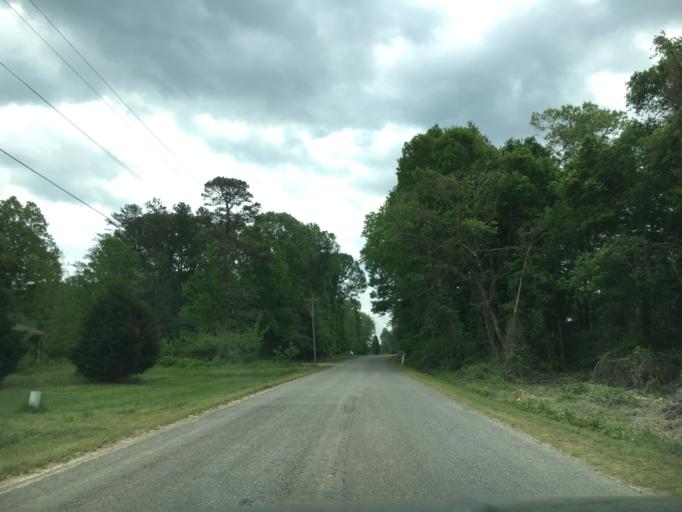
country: US
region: Virginia
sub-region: Halifax County
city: Halifax
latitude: 36.8010
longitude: -78.9440
